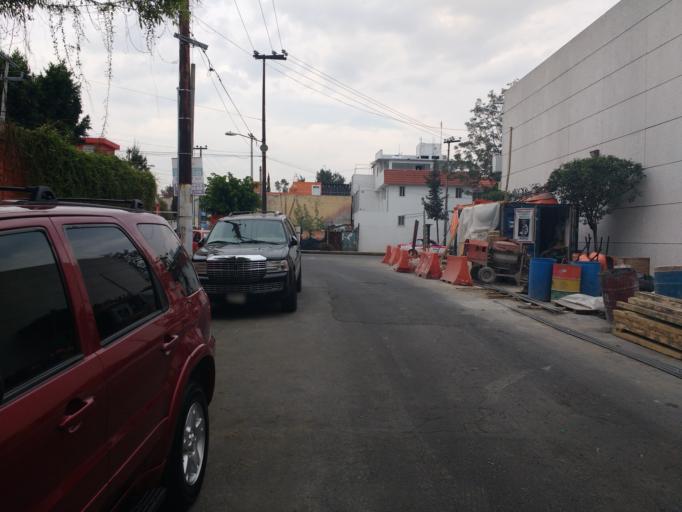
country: MX
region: Mexico City
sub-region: Iztacalco
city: Iztacalco
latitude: 19.3853
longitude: -99.0834
